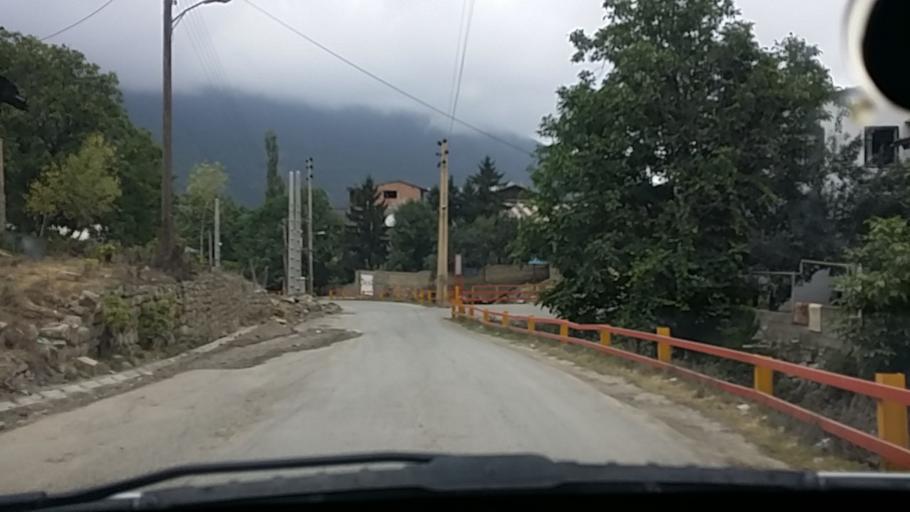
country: IR
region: Mazandaran
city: `Abbasabad
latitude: 36.4821
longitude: 51.1371
